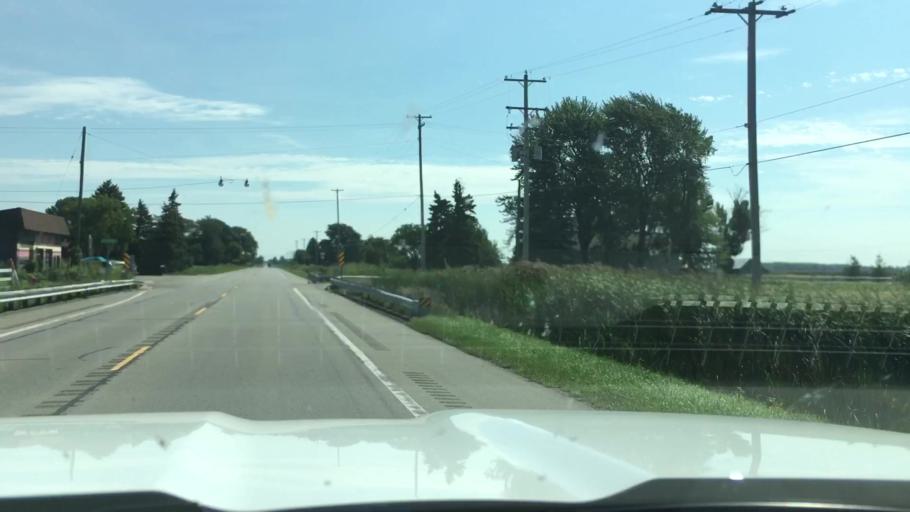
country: US
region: Michigan
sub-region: Bay County
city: Essexville
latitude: 43.5906
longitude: -83.7506
